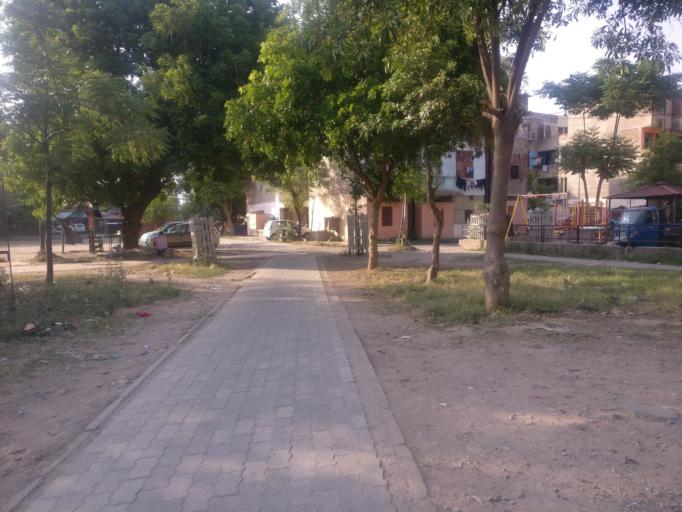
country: IN
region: Punjab
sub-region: Ajitgarh
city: Mohali
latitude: 30.7341
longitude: 76.7211
